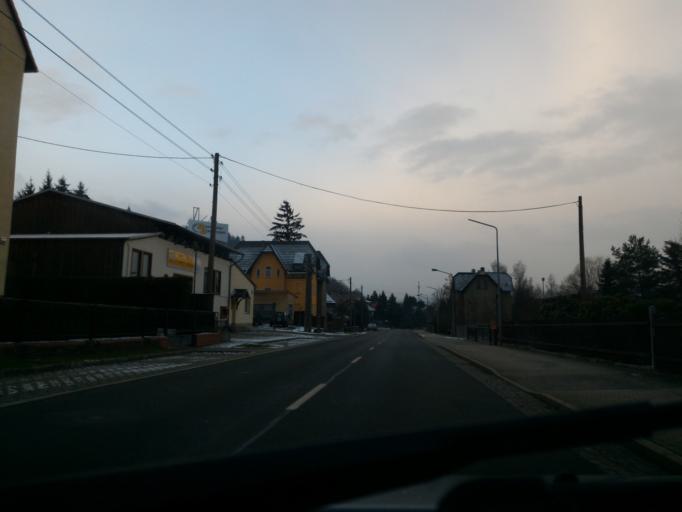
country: DE
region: Saxony
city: Seifhennersdorf
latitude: 50.9281
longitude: 14.6113
